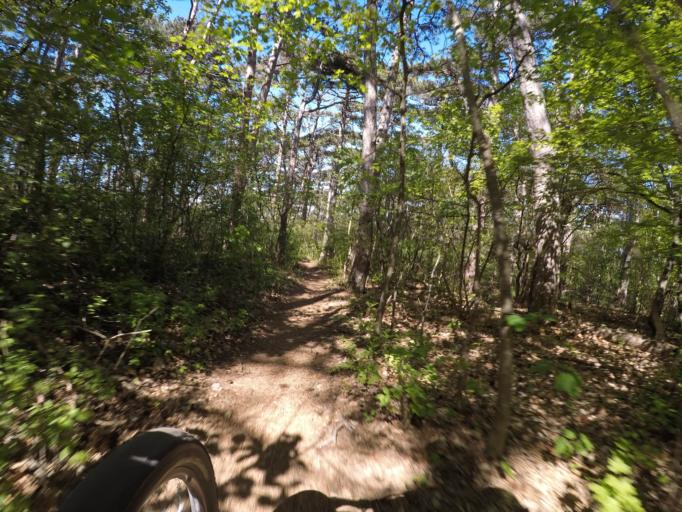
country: AT
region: Lower Austria
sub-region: Politischer Bezirk Modling
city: Gumpoldskirchen
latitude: 48.0658
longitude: 16.2816
